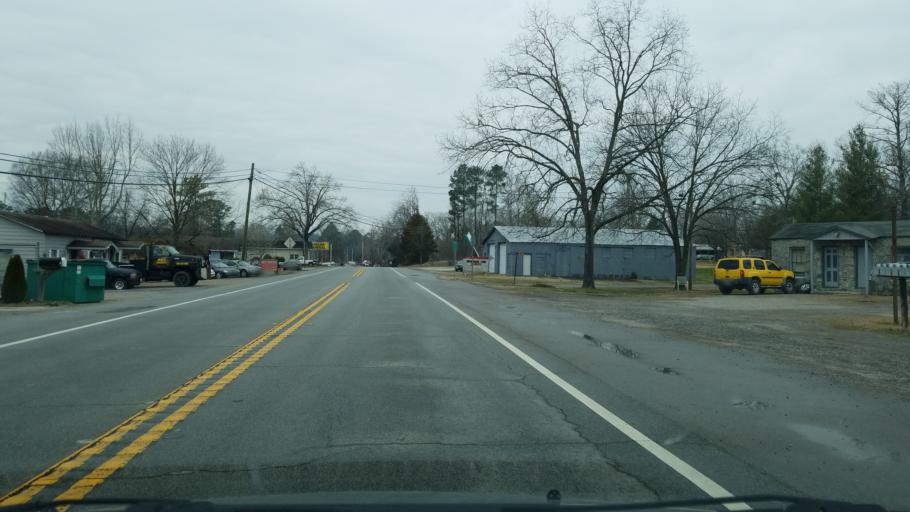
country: US
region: Georgia
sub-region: Catoosa County
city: Indian Springs
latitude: 34.9600
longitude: -85.1662
